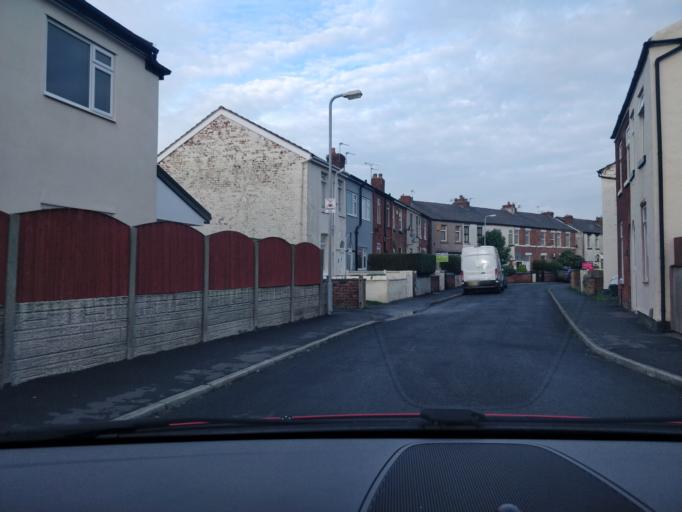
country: GB
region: England
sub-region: Sefton
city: Southport
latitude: 53.6437
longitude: -2.9945
